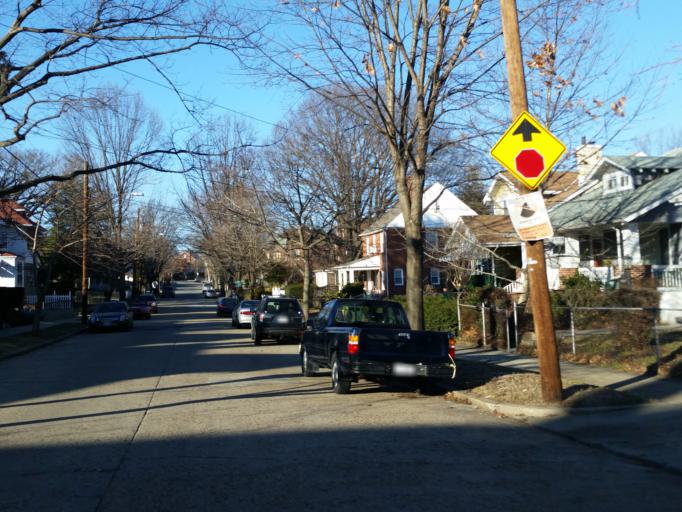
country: US
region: Maryland
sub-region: Montgomery County
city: Takoma Park
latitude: 38.9691
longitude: -77.0242
